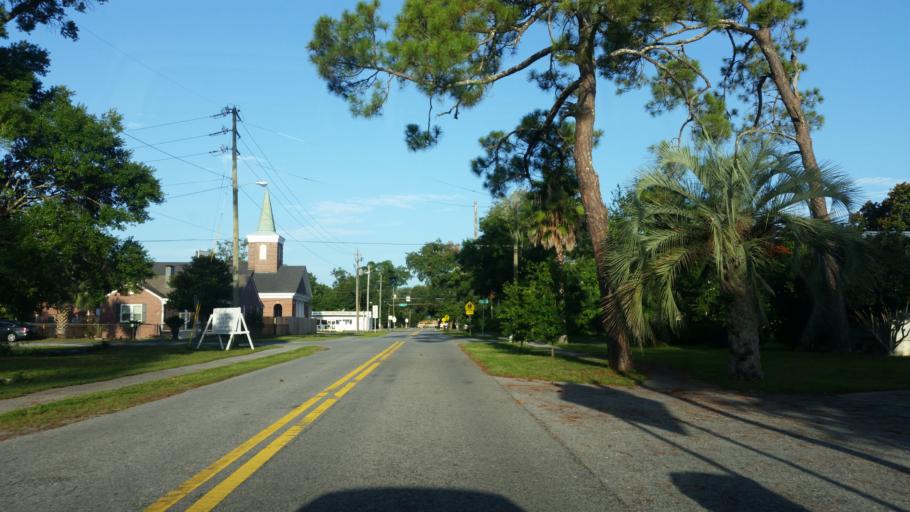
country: US
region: Florida
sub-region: Escambia County
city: Warrington
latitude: 30.3828
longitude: -87.2764
